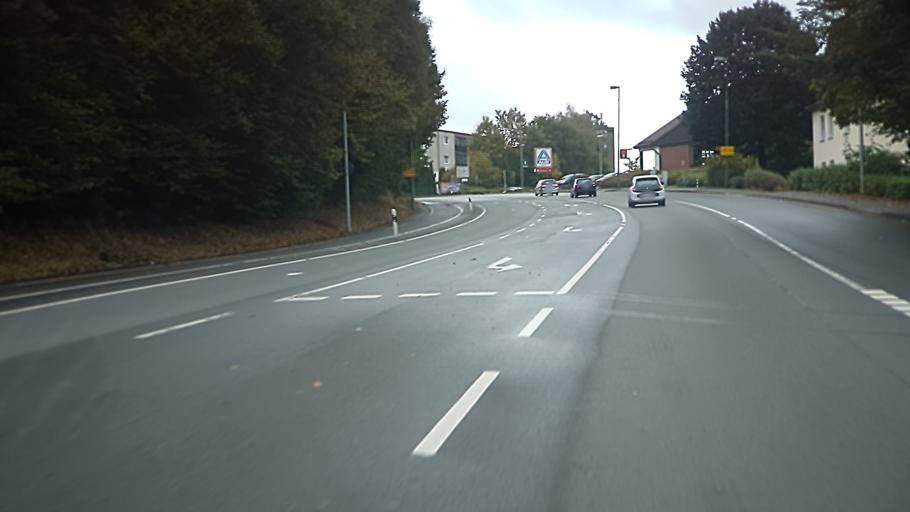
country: DE
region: North Rhine-Westphalia
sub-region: Regierungsbezirk Arnsberg
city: Luedenscheid
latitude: 51.2059
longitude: 7.6541
